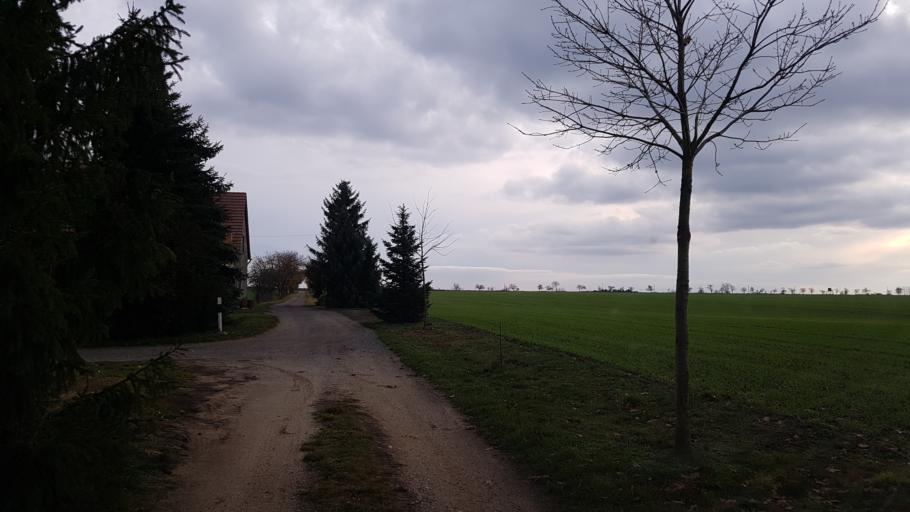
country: DE
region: Brandenburg
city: Trobitz
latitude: 51.6660
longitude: 13.4198
